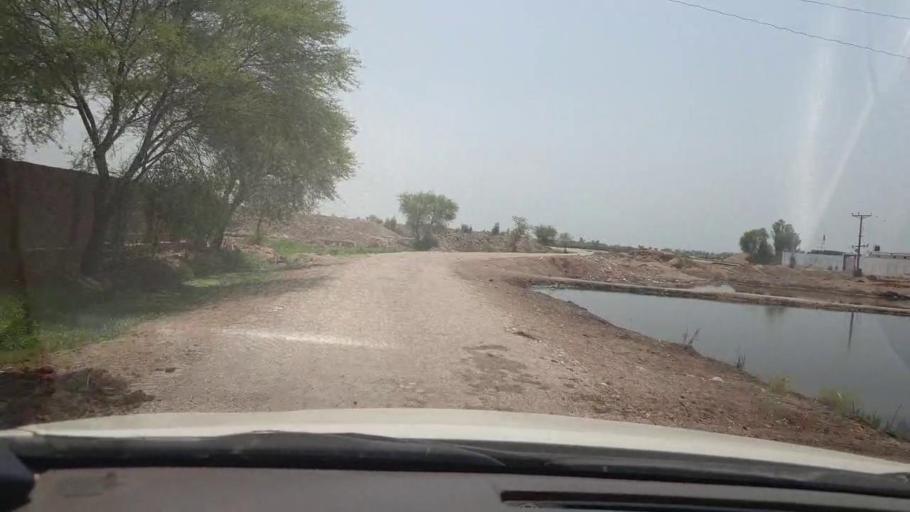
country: PK
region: Sindh
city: Garhi Yasin
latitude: 27.9085
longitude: 68.5536
